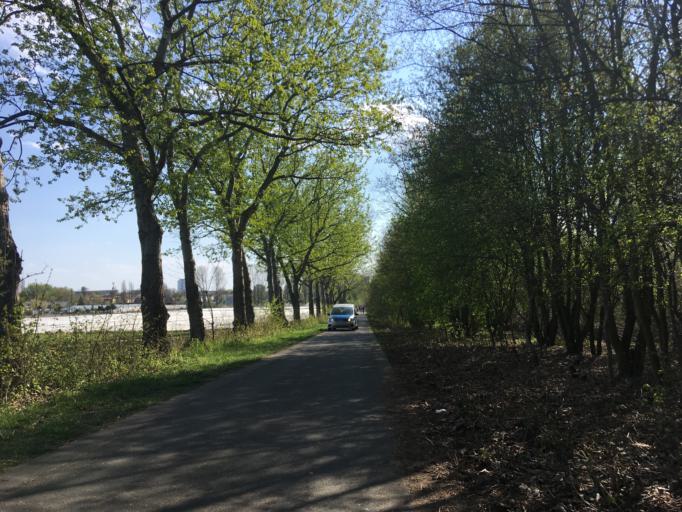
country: DE
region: Berlin
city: Wartenberg
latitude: 52.5831
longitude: 13.5148
